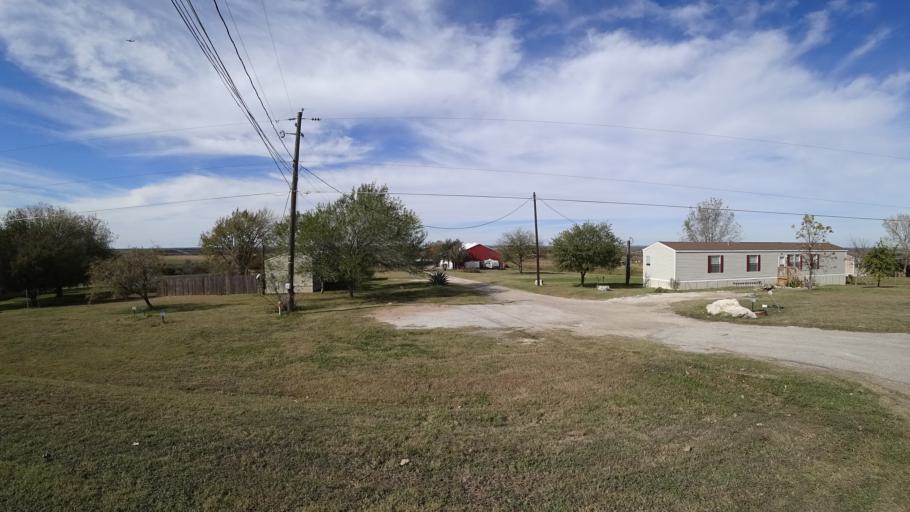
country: US
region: Texas
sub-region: Travis County
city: Onion Creek
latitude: 30.1179
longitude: -97.7450
